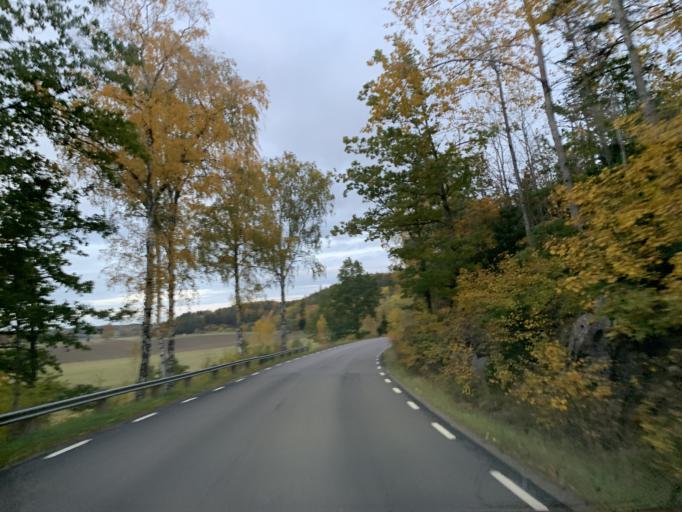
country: SE
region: Stockholm
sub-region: Nynashamns Kommun
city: Osmo
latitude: 58.9688
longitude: 17.7727
